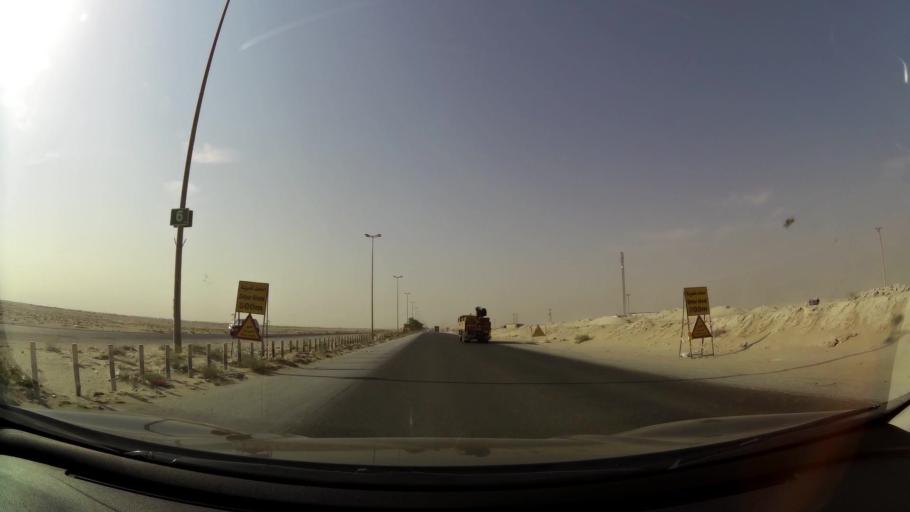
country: KW
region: Al Ahmadi
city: Al Ahmadi
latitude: 28.9048
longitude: 48.0930
